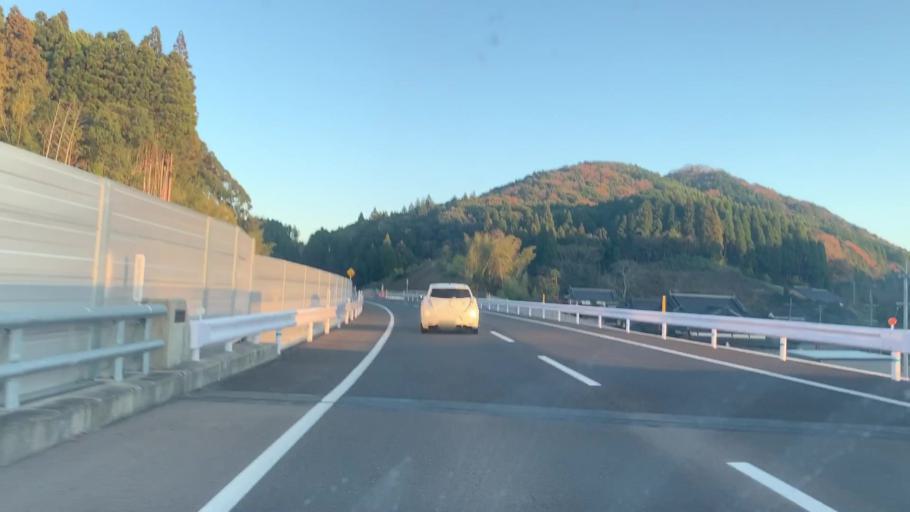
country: JP
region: Saga Prefecture
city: Takeocho-takeo
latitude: 33.2578
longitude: 129.9754
